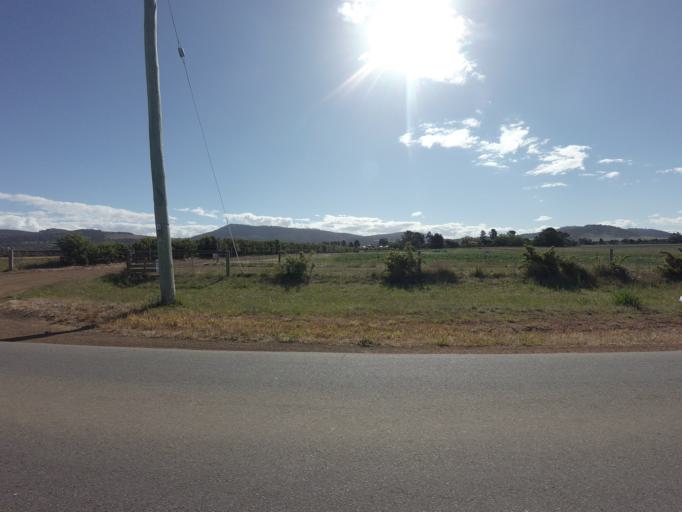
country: AU
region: Tasmania
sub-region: Clarence
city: Cambridge
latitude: -42.7562
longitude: 147.4163
